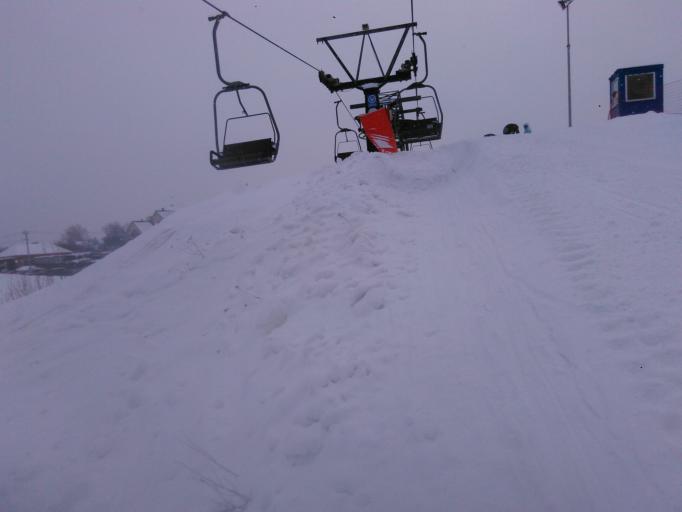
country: RU
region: Moskovskaya
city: Yakhroma
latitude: 56.2510
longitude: 37.4397
